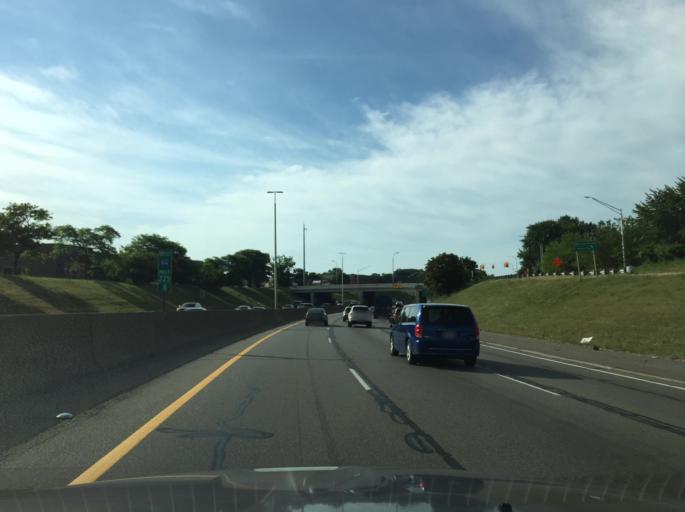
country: US
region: Michigan
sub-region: Wayne County
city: Grosse Pointe Woods
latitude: 42.4520
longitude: -82.9187
